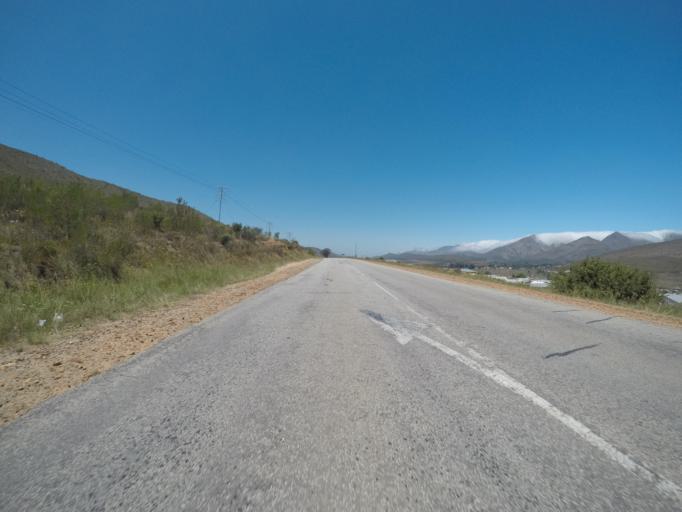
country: ZA
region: Eastern Cape
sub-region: Cacadu District Municipality
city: Kareedouw
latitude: -33.8272
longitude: 23.8771
